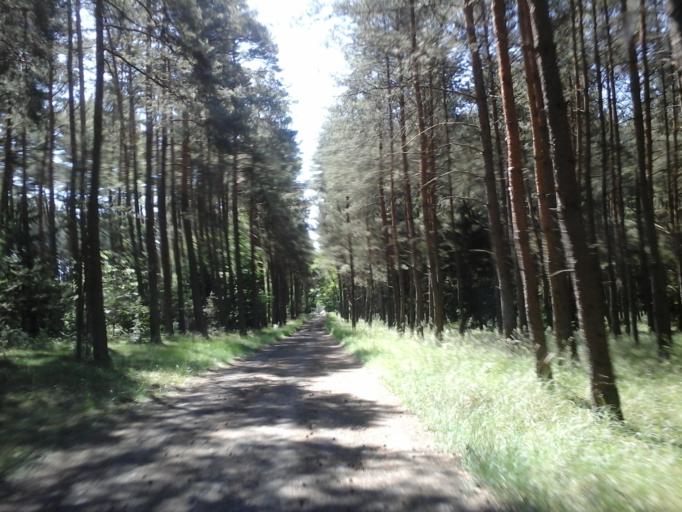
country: PL
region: West Pomeranian Voivodeship
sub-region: Powiat walecki
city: Czlopa
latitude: 53.1473
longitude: 15.9701
